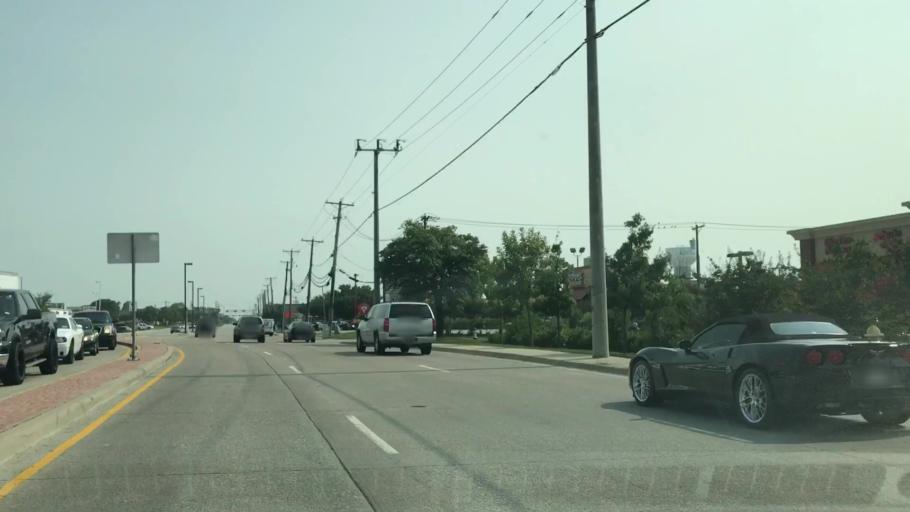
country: US
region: Texas
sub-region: Dallas County
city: Rowlett
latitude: 32.9073
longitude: -96.5695
